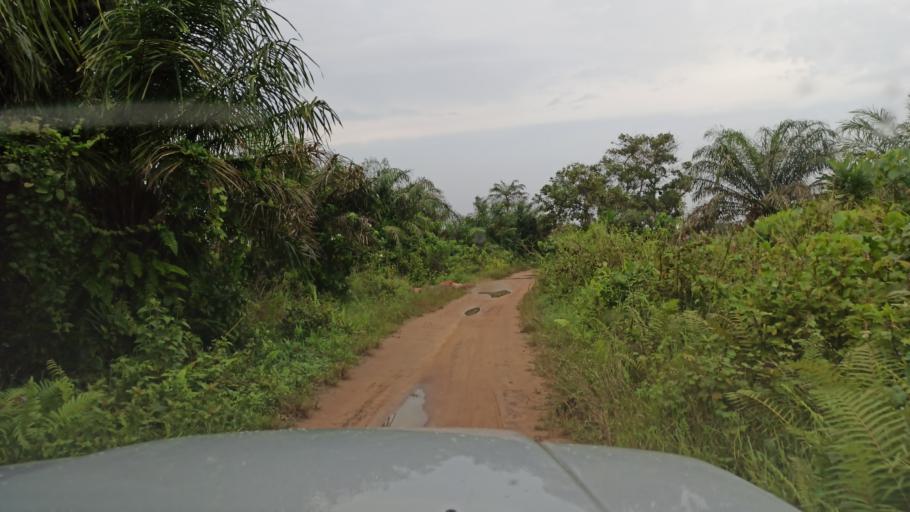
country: BJ
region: Queme
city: Porto-Novo
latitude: 6.4585
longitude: 2.6747
